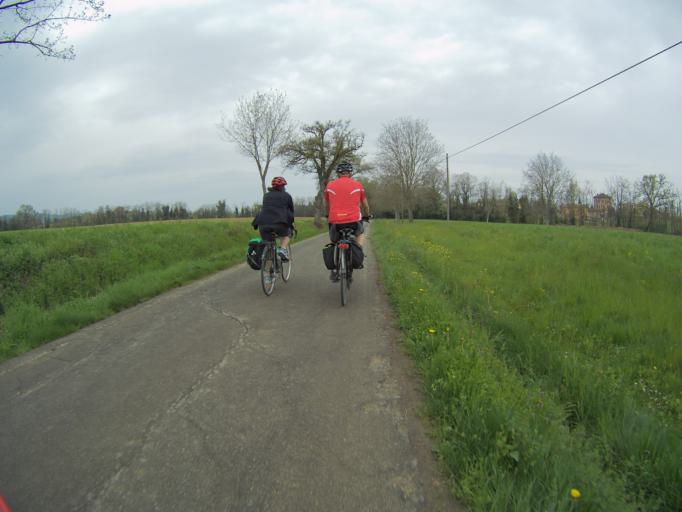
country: IT
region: Emilia-Romagna
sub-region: Provincia di Reggio Emilia
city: San Bartolomeo
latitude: 44.6604
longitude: 10.5299
